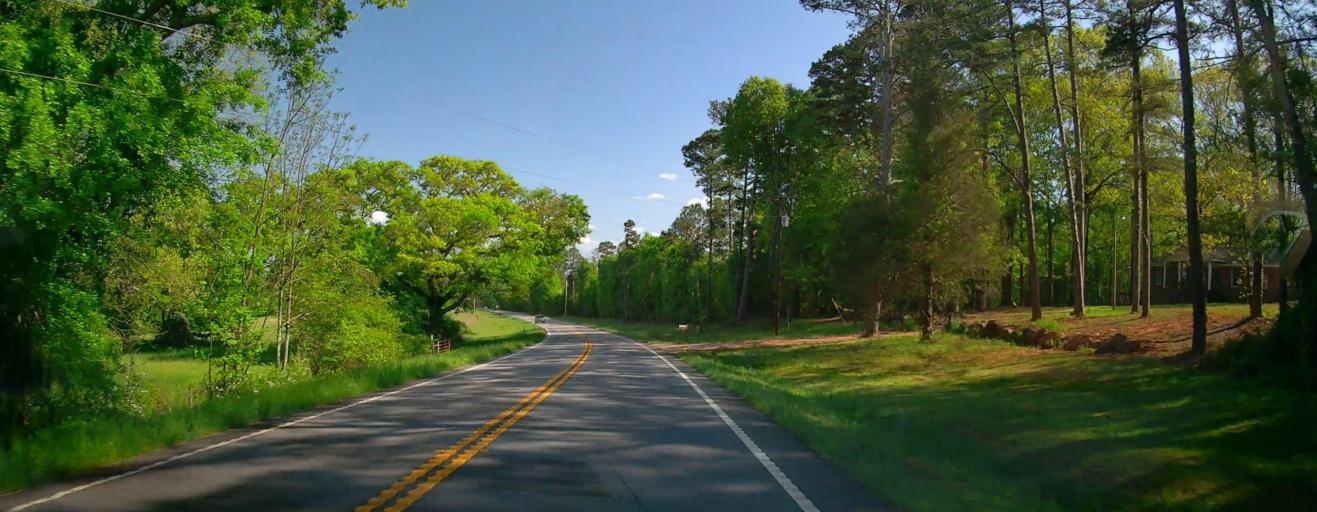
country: US
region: Georgia
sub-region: Morgan County
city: Madison
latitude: 33.6486
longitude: -83.4973
